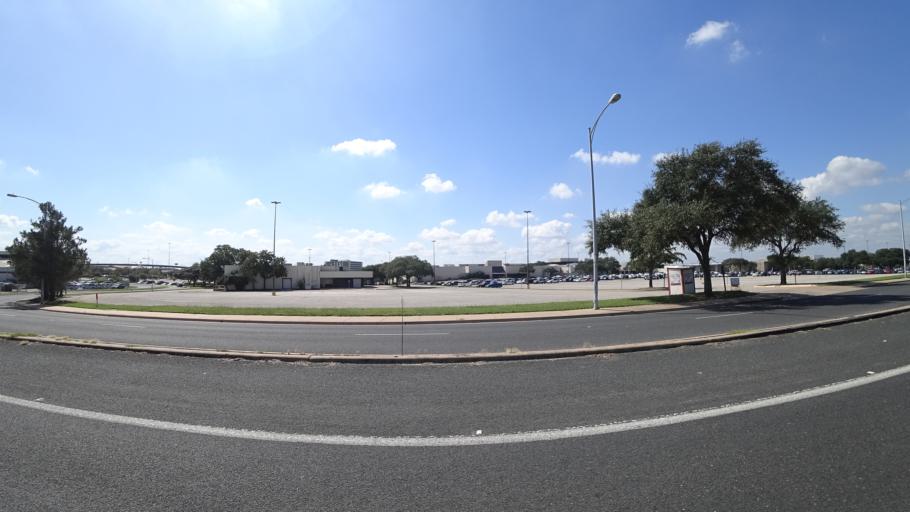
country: US
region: Texas
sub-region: Travis County
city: Austin
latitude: 30.3285
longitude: -97.7107
